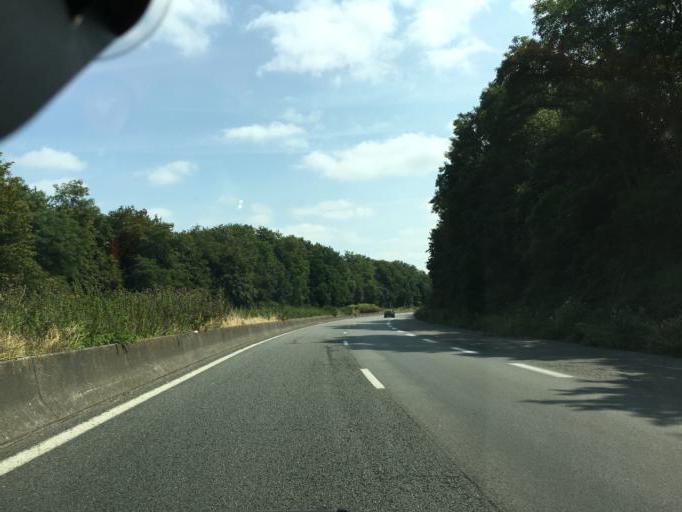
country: FR
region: Nord-Pas-de-Calais
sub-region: Departement du Nord
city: Lourches
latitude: 50.3217
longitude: 3.3648
